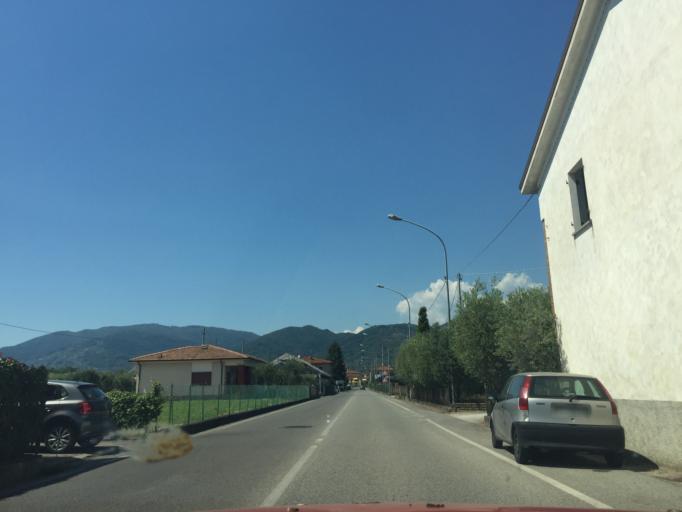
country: IT
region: Tuscany
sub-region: Provincia di Pistoia
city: Pescia
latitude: 43.8749
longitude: 10.6912
